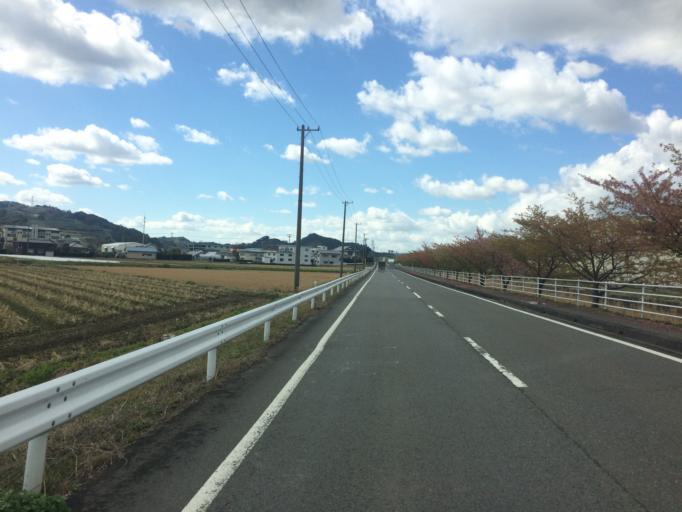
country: JP
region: Shizuoka
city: Shimada
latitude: 34.7777
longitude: 138.2245
